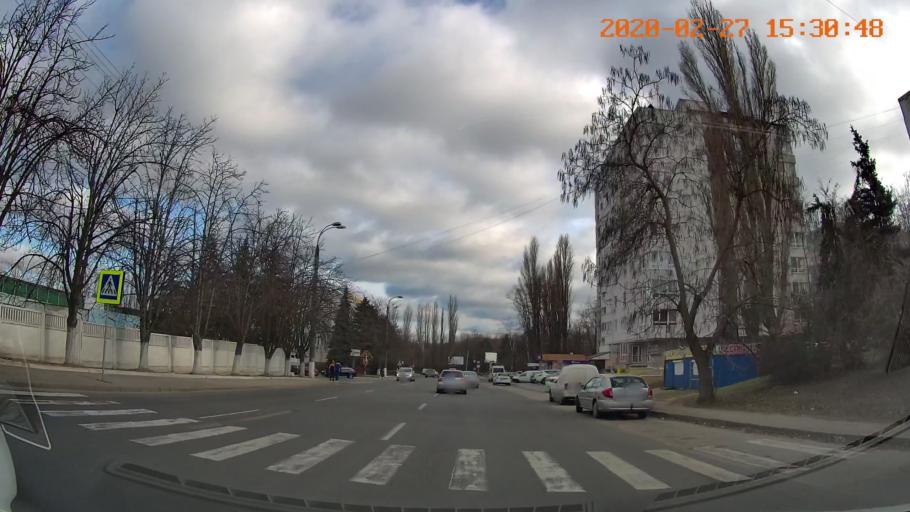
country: MD
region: Chisinau
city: Chisinau
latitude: 46.9801
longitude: 28.8825
